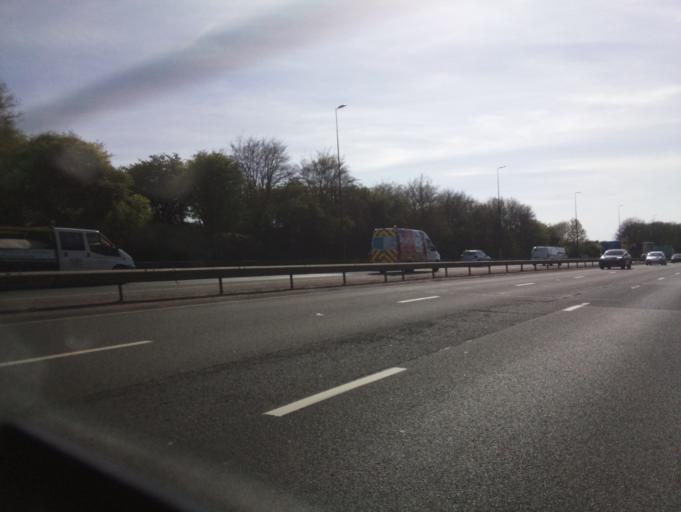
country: GB
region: Wales
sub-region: Monmouthshire
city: Magor
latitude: 51.5871
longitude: -2.8269
